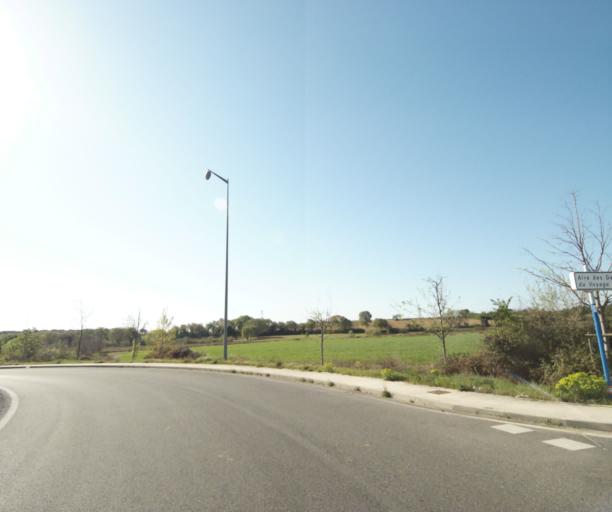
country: FR
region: Languedoc-Roussillon
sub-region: Departement de l'Herault
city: Le Cres
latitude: 43.6302
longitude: 3.9349
